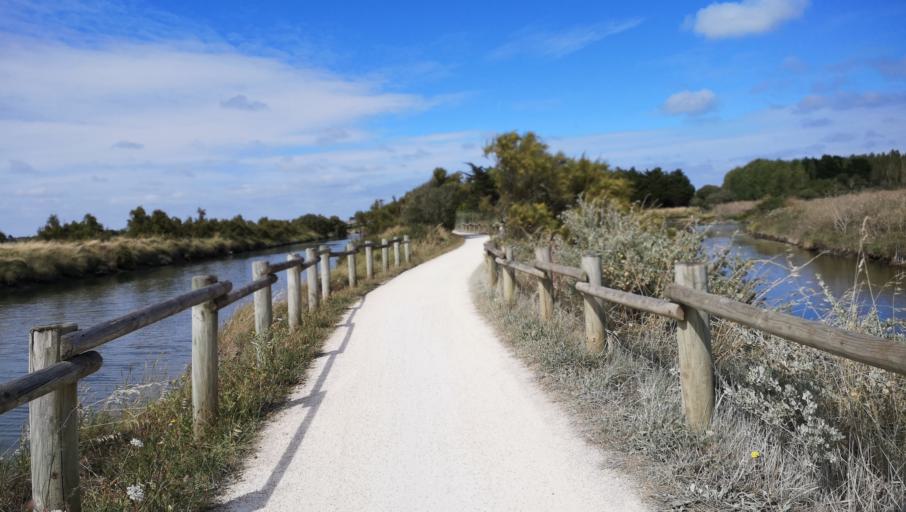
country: FR
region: Pays de la Loire
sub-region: Departement de la Vendee
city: Olonne-sur-Mer
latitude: 46.5327
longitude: -1.8072
